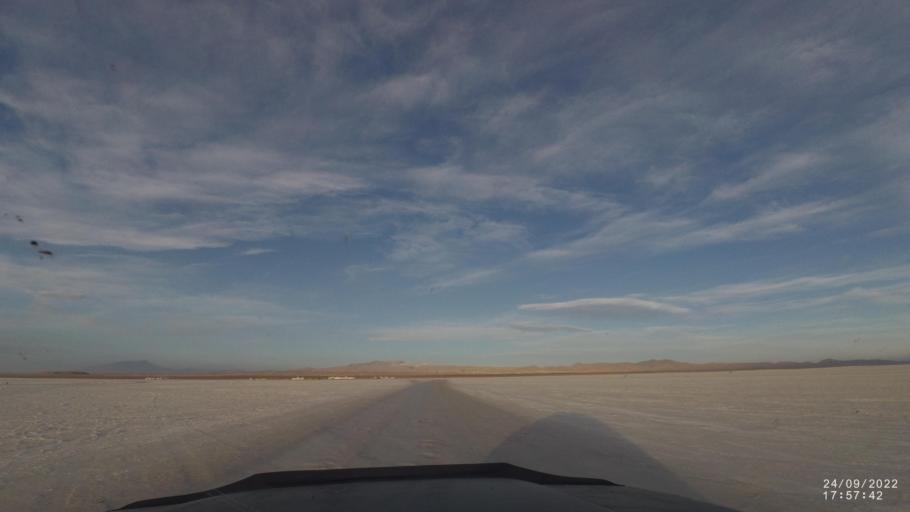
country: BO
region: Potosi
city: Colchani
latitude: -20.3192
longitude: -66.9878
